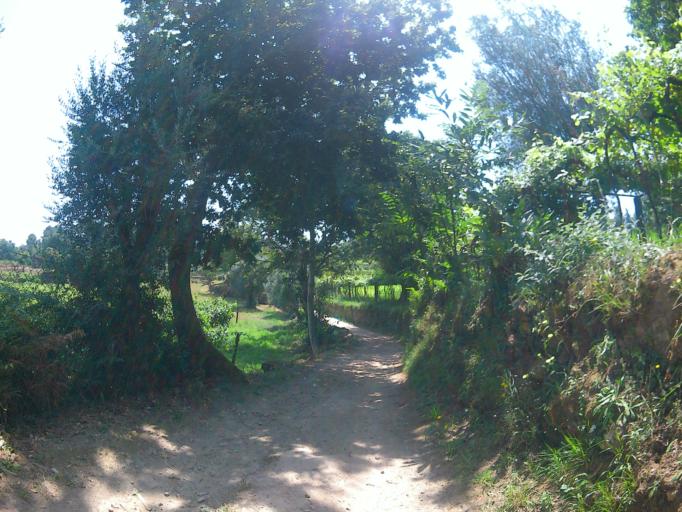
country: PT
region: Viana do Castelo
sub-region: Ponte de Lima
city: Ponte de Lima
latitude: 41.7743
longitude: -8.5676
